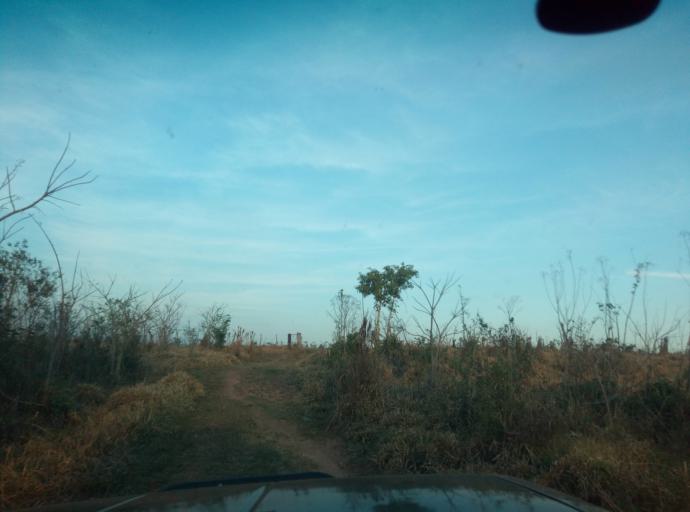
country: PY
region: Caaguazu
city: Yhu
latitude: -25.2002
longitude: -56.1087
